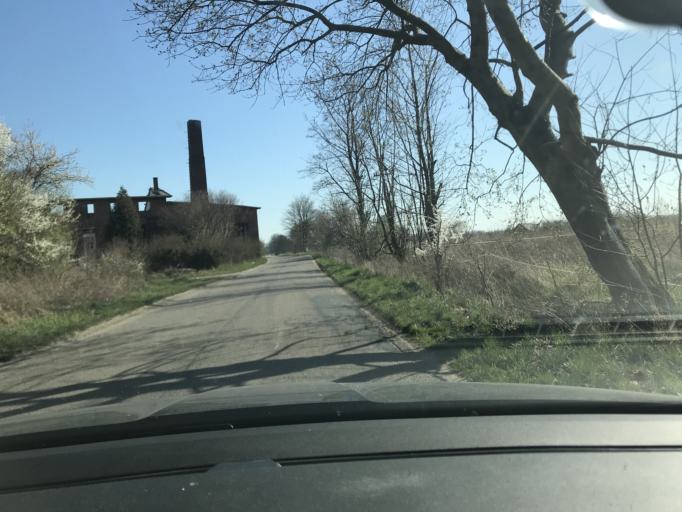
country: PL
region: Pomeranian Voivodeship
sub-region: Powiat nowodworski
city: Sztutowo
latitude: 54.3175
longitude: 19.1590
